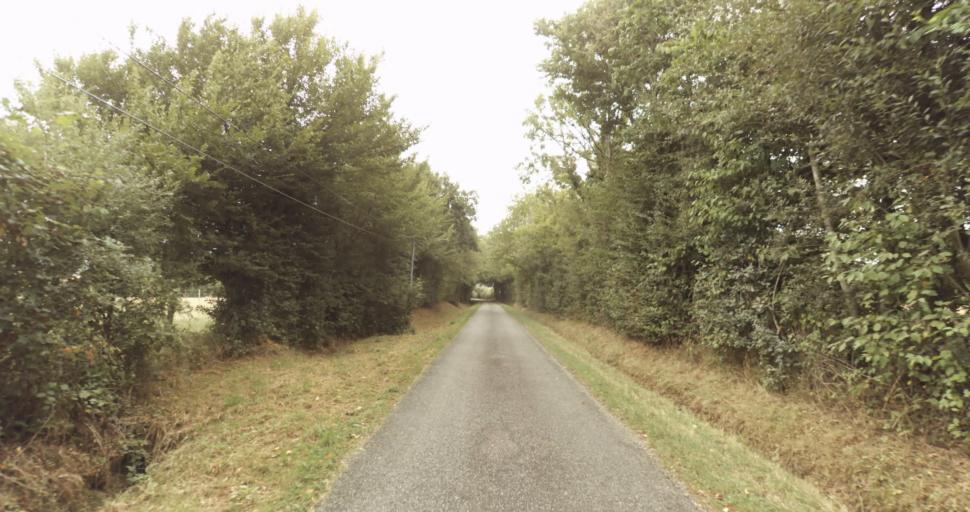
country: FR
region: Lower Normandy
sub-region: Departement de l'Orne
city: Sainte-Gauburge-Sainte-Colombe
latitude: 48.7148
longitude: 0.4598
